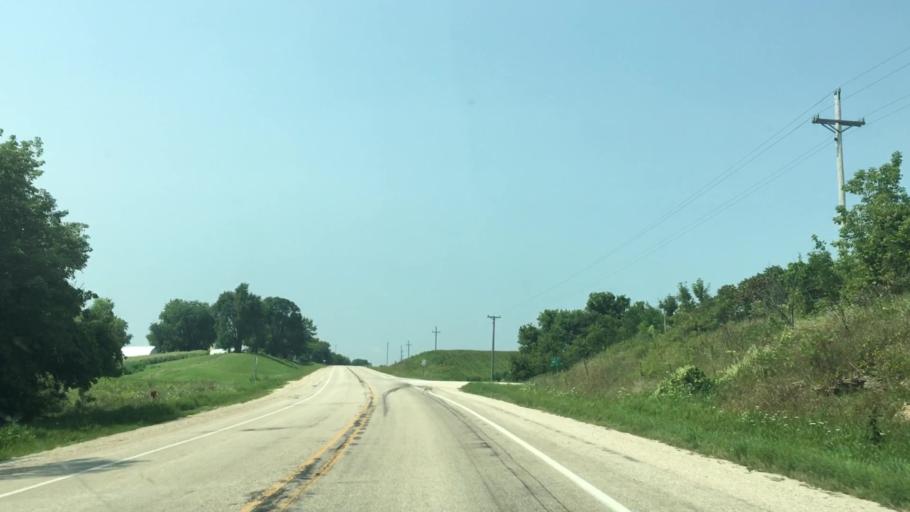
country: US
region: Iowa
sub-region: Fayette County
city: West Union
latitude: 43.0796
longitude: -91.8413
